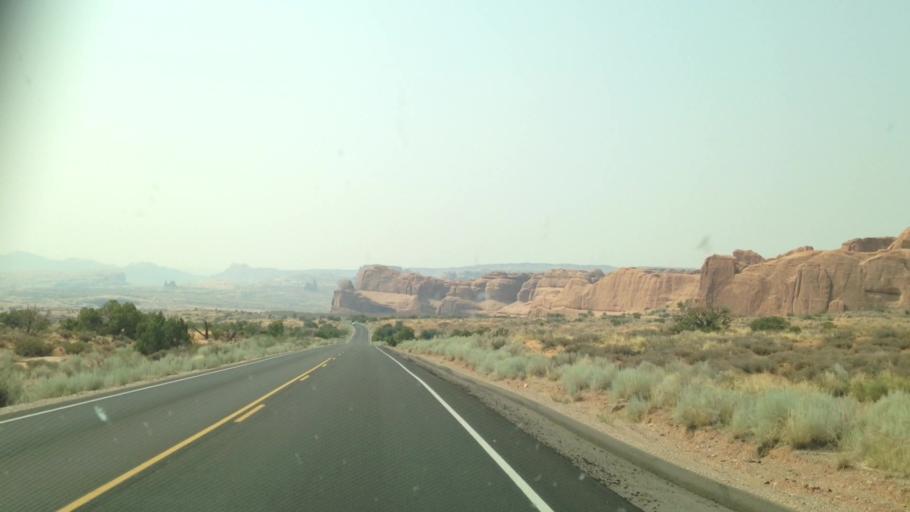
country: US
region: Utah
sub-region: Grand County
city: Moab
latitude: 38.6765
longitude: -109.5874
